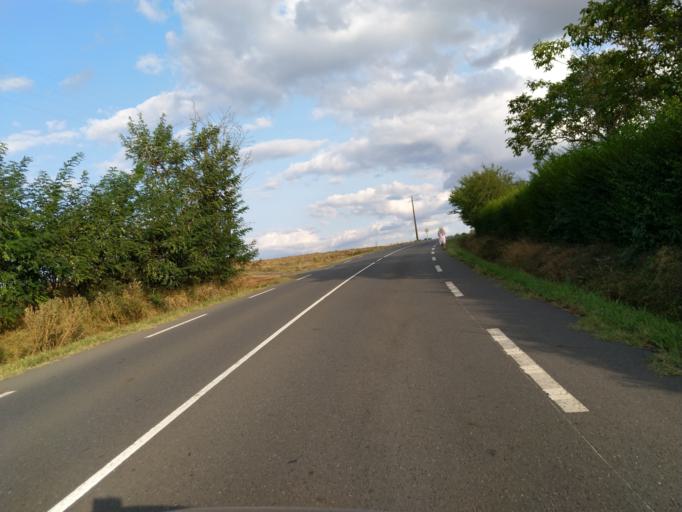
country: FR
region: Midi-Pyrenees
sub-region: Departement du Tarn
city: Puygouzon
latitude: 43.9133
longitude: 2.1925
